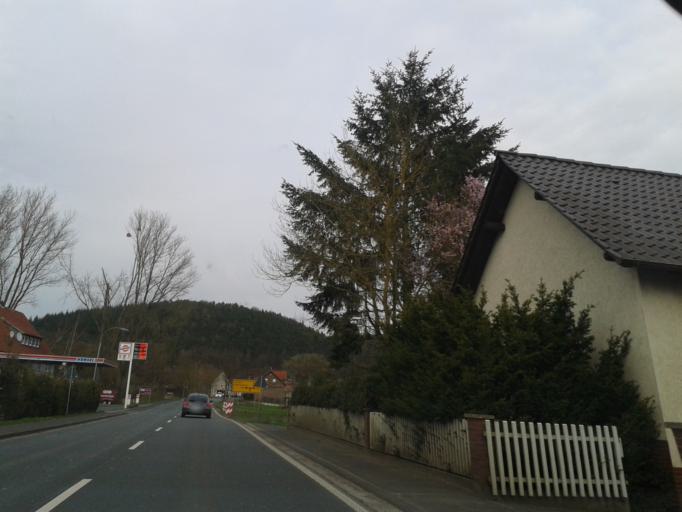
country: DE
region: Hesse
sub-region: Regierungsbezirk Giessen
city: Colbe
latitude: 50.8730
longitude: 8.7709
